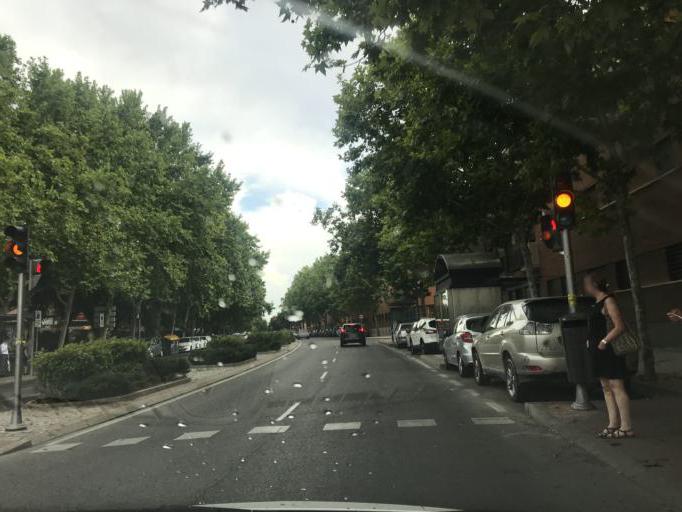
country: ES
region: Madrid
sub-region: Provincia de Madrid
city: Barajas de Madrid
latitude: 40.4754
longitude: -3.5825
